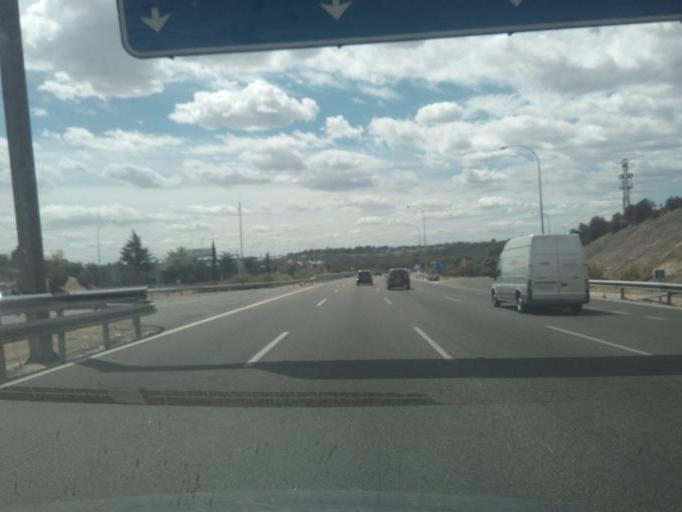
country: ES
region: Madrid
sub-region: Provincia de Madrid
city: Fuencarral-El Pardo
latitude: 40.4836
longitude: -3.7439
